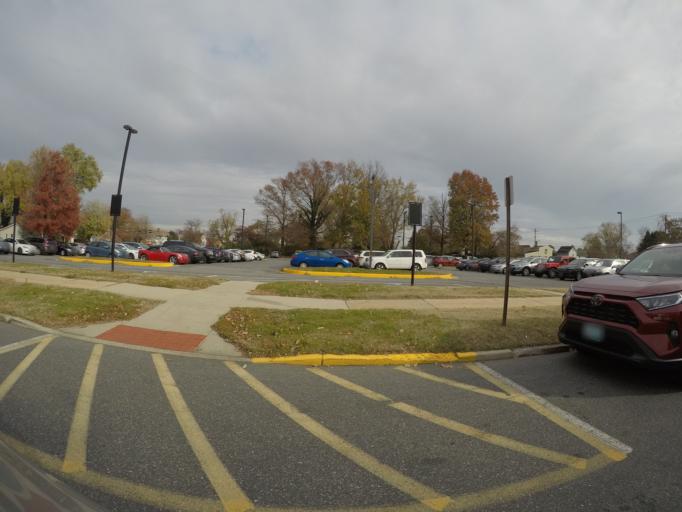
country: US
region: Maryland
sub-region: Harford County
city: Havre de Grace
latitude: 39.5431
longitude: -76.0897
